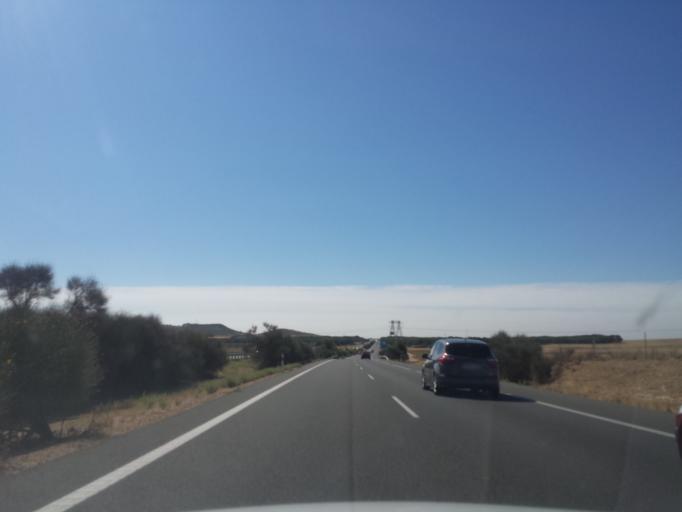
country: ES
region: Castille and Leon
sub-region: Provincia de Valladolid
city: Bercero
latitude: 41.5559
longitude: -5.0805
